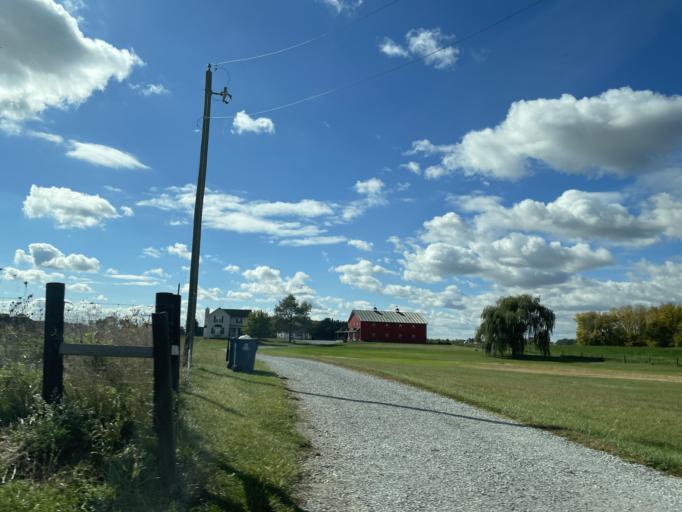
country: US
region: Indiana
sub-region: Whitley County
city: Churubusco
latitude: 41.1218
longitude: -85.2745
